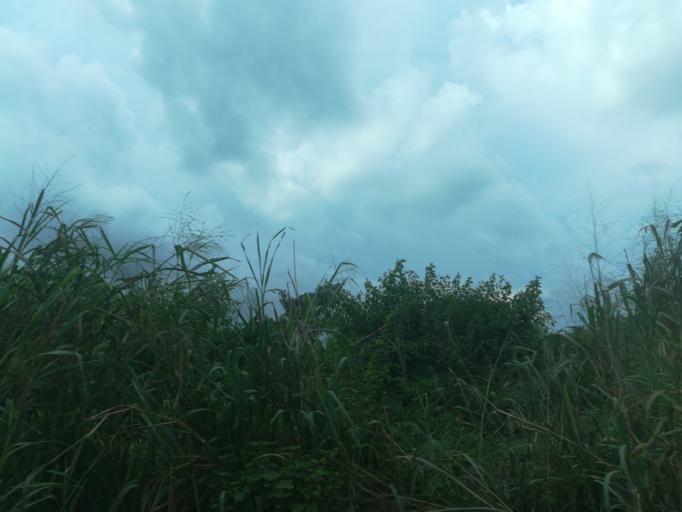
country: NG
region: Lagos
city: Ikorodu
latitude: 6.6419
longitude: 3.5515
